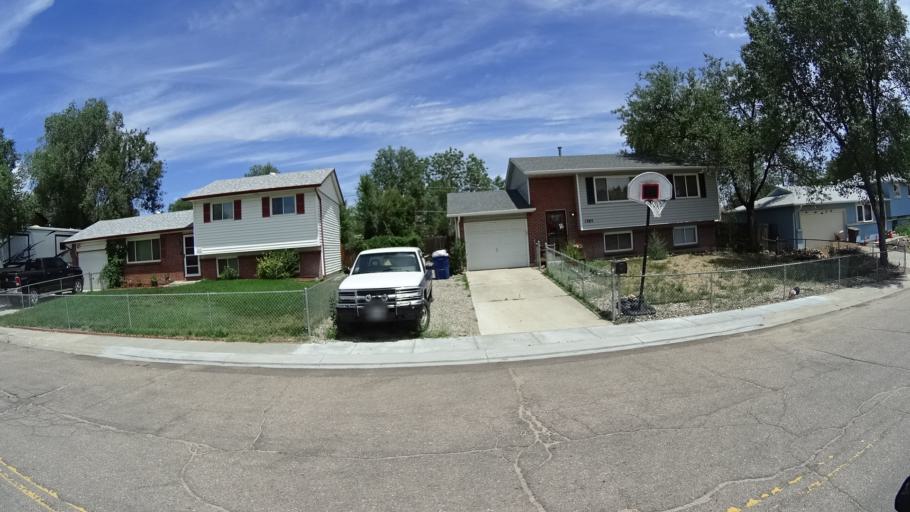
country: US
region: Colorado
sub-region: El Paso County
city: Security-Widefield
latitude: 38.7325
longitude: -104.7310
